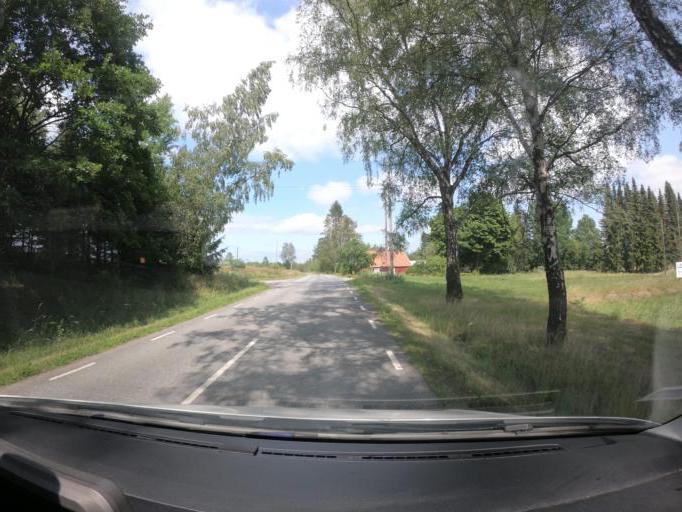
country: SE
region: Skane
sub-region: Hassleholms Kommun
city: Sosdala
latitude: 56.0476
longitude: 13.6960
